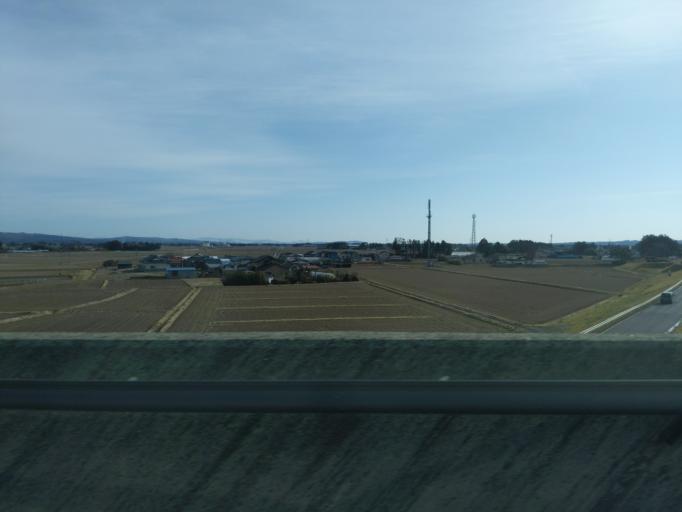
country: JP
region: Miyagi
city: Furukawa
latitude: 38.5894
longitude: 140.9749
